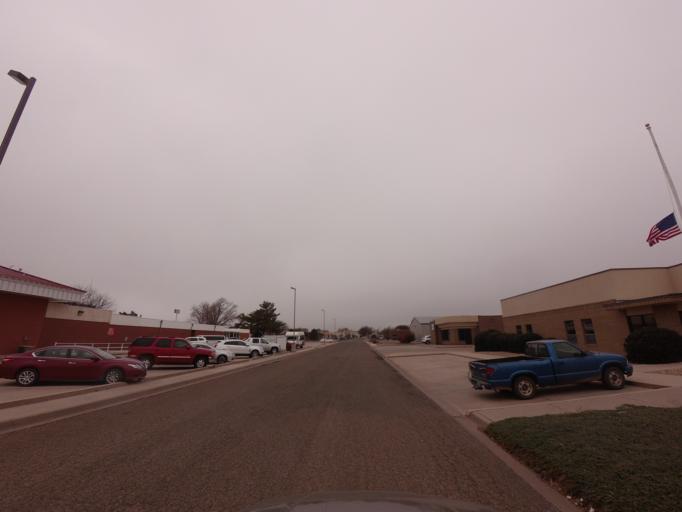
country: US
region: New Mexico
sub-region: Curry County
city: Clovis
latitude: 34.4231
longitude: -103.1932
